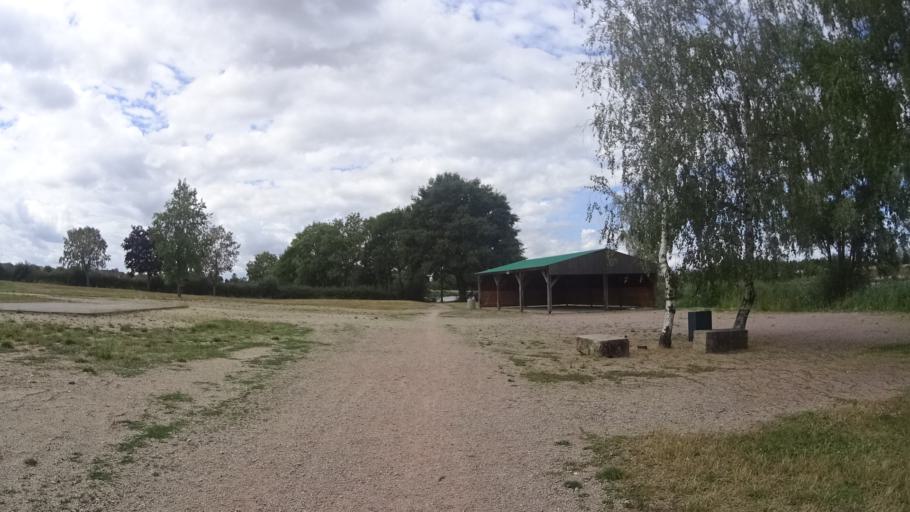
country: FR
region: Bourgogne
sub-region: Departement de Saone-et-Loire
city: Saint-Leu
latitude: 46.7367
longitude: 4.4860
